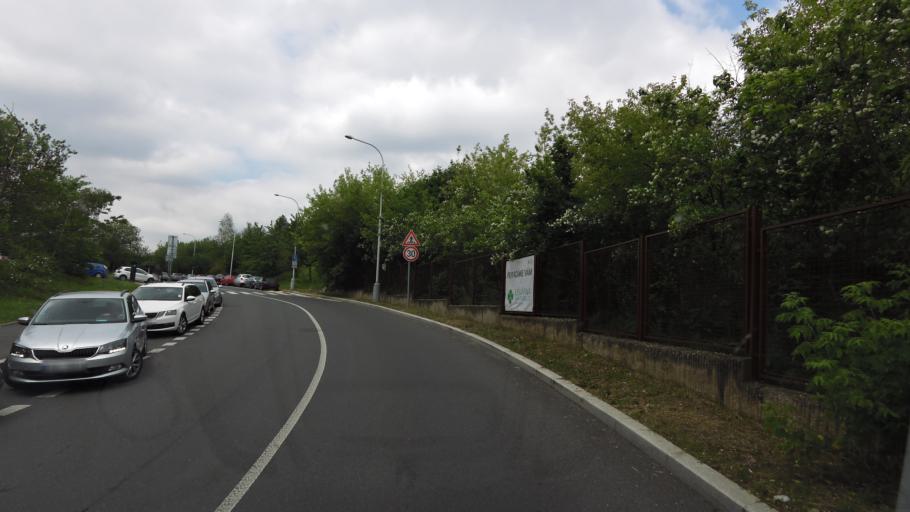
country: CZ
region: Praha
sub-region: Praha 1
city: Mala Strana
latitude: 50.0748
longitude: 14.3524
